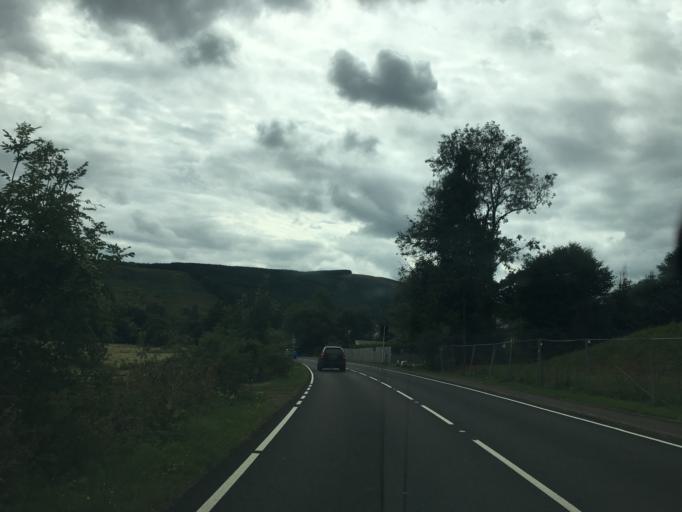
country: GB
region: Scotland
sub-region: Stirling
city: Callander
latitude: 56.3822
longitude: -4.2869
